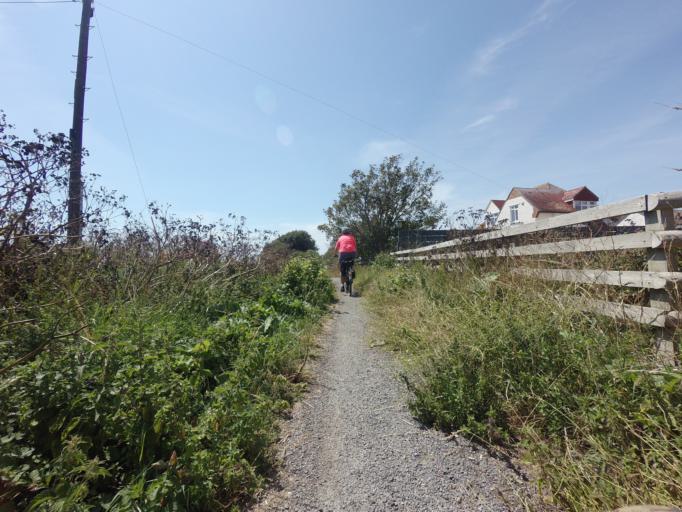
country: GB
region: England
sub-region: Kent
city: Lydd
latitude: 50.9349
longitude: 0.8507
